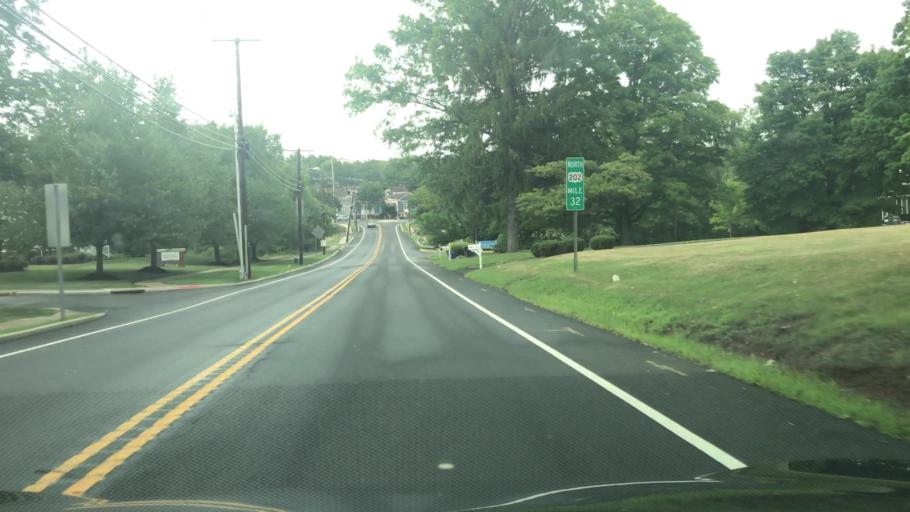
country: US
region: New Jersey
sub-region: Somerset County
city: Bedminster
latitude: 40.6783
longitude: -74.6456
